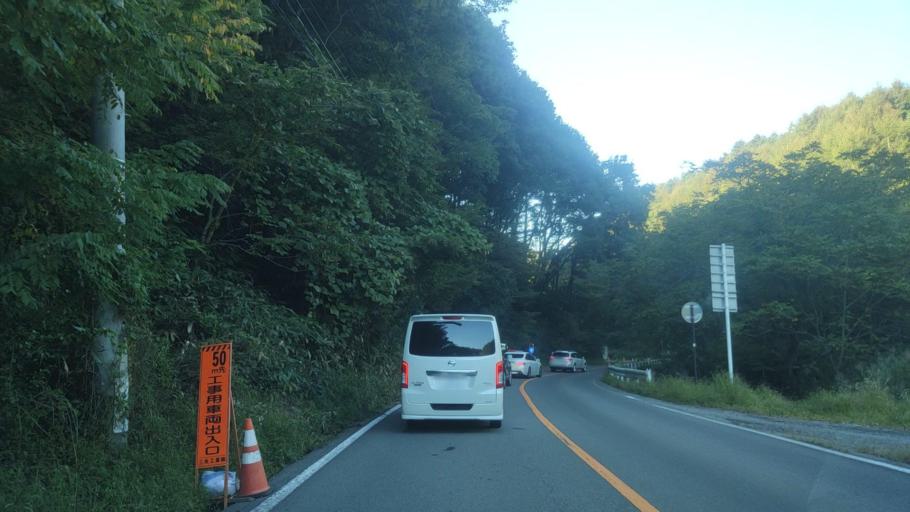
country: JP
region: Nagano
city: Kamimaruko
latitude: 36.2400
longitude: 138.3047
